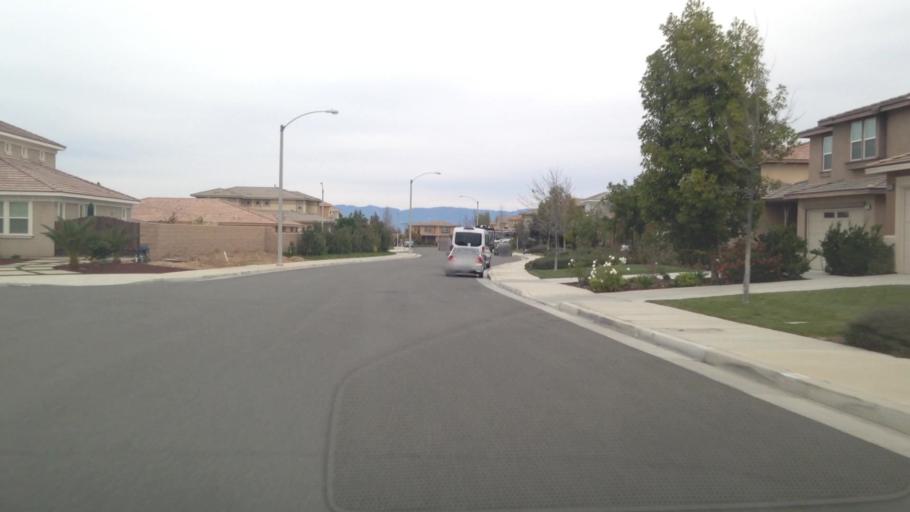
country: US
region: California
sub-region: Riverside County
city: Woodcrest
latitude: 33.8805
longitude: -117.3451
